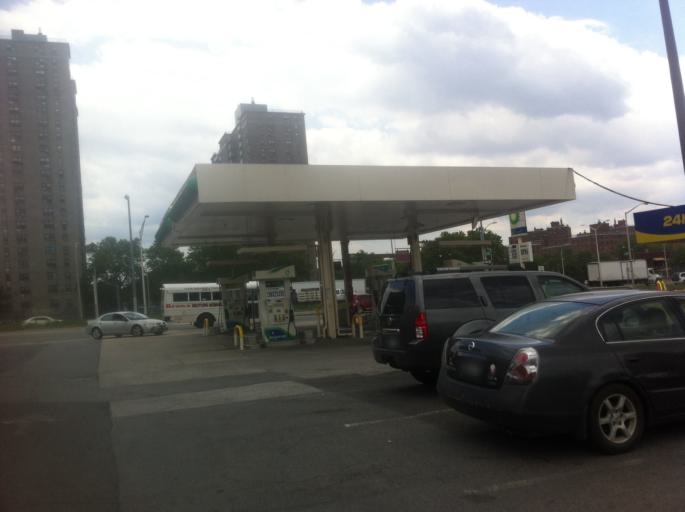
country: US
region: New York
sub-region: Bronx
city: The Bronx
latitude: 40.8265
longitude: -73.8618
